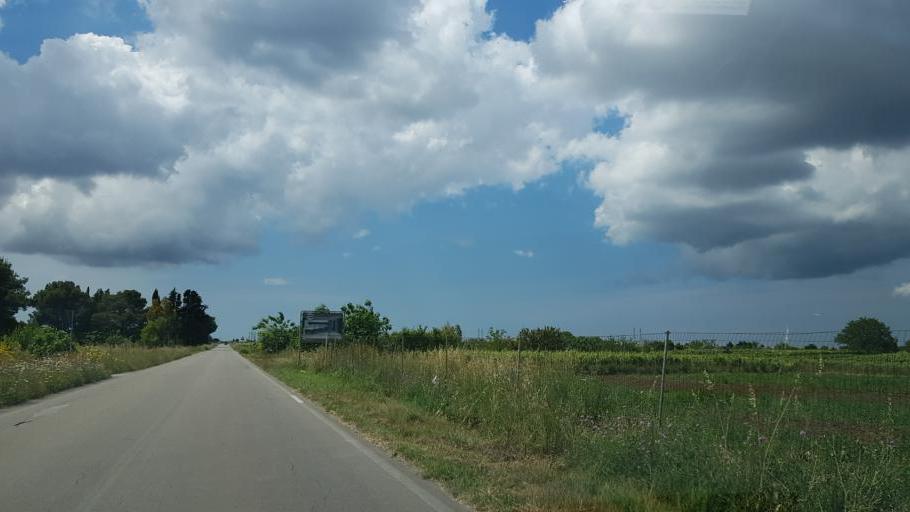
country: IT
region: Apulia
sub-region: Provincia di Brindisi
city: San Pancrazio Salentino
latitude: 40.4050
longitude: 17.8359
